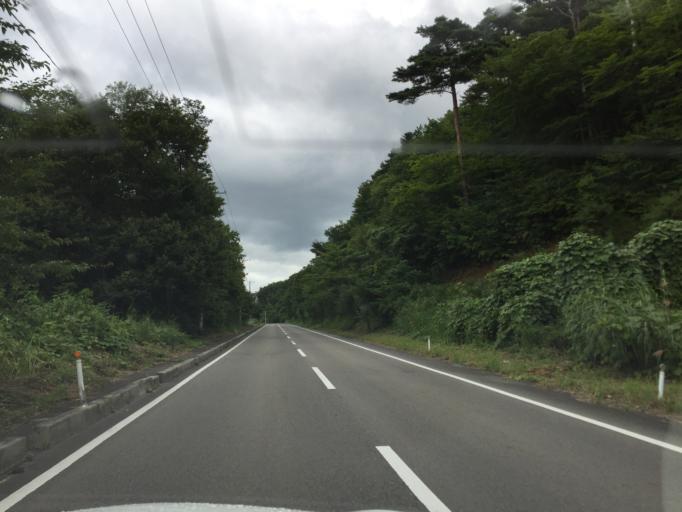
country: JP
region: Fukushima
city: Miharu
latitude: 37.4411
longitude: 140.5278
